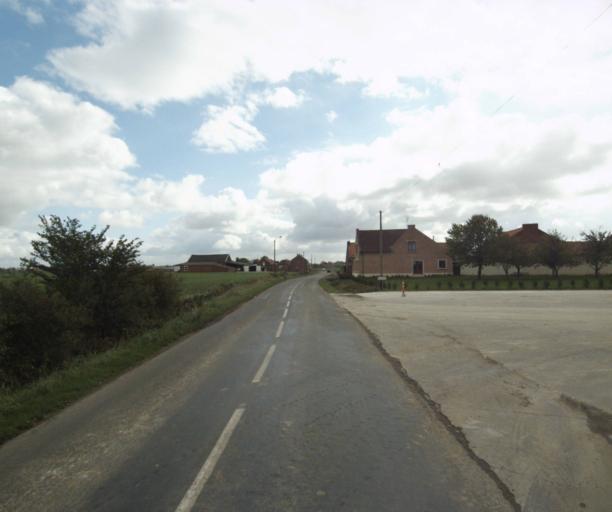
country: FR
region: Nord-Pas-de-Calais
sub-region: Departement du Nord
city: Frelinghien
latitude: 50.6901
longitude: 2.9434
